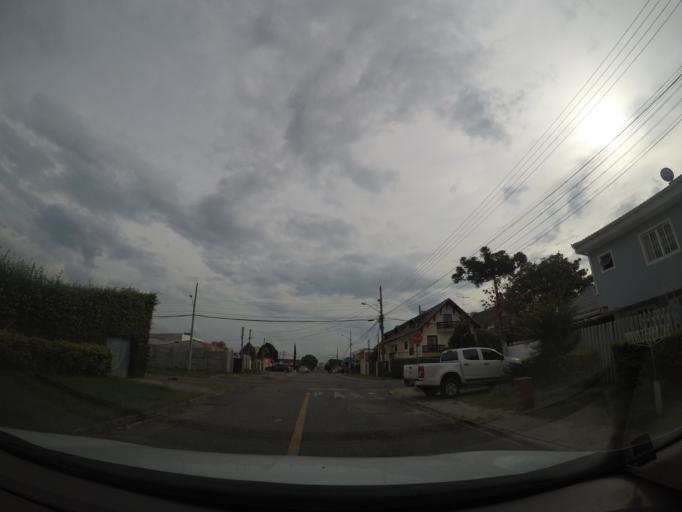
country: BR
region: Parana
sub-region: Sao Jose Dos Pinhais
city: Sao Jose dos Pinhais
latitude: -25.5061
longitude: -49.2630
